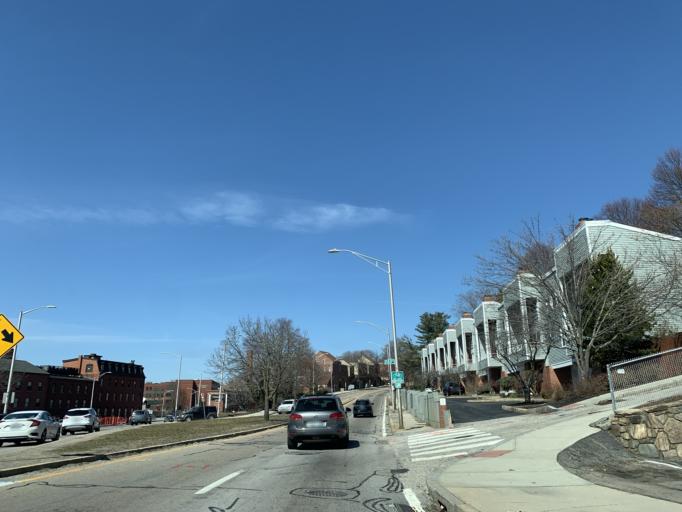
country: US
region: Rhode Island
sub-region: Providence County
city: Providence
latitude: 41.8318
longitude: -71.4106
